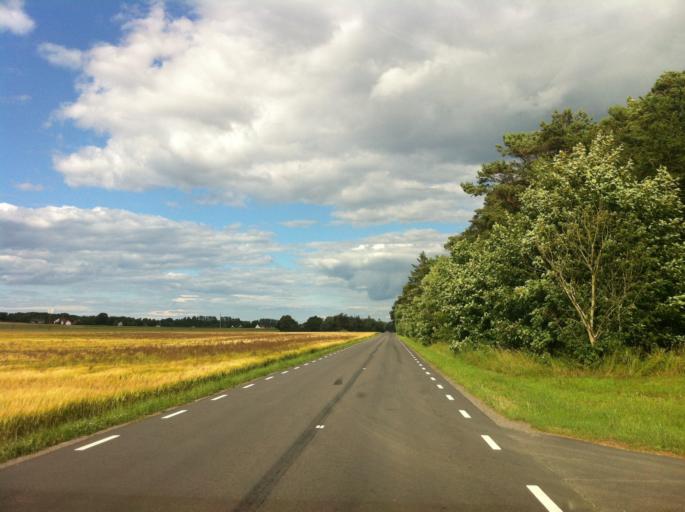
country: SE
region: Skane
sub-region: Simrishamns Kommun
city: Simrishamn
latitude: 55.4323
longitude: 14.2246
